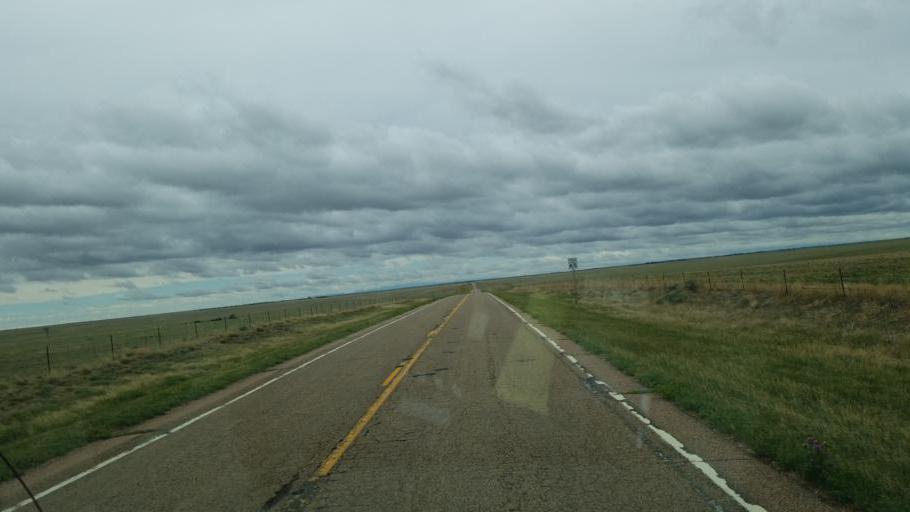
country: US
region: Colorado
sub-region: Lincoln County
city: Limon
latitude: 38.8390
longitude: -103.8915
